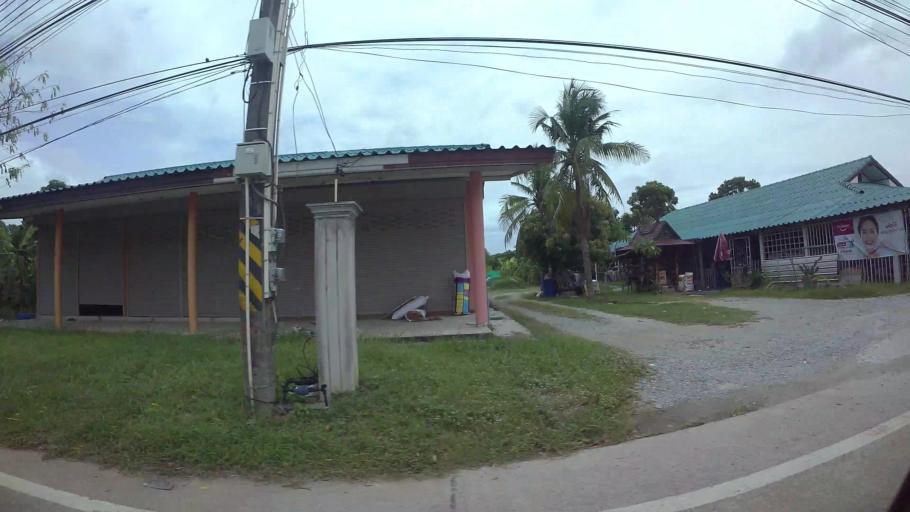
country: TH
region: Chon Buri
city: Si Racha
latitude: 13.1668
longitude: 100.9728
